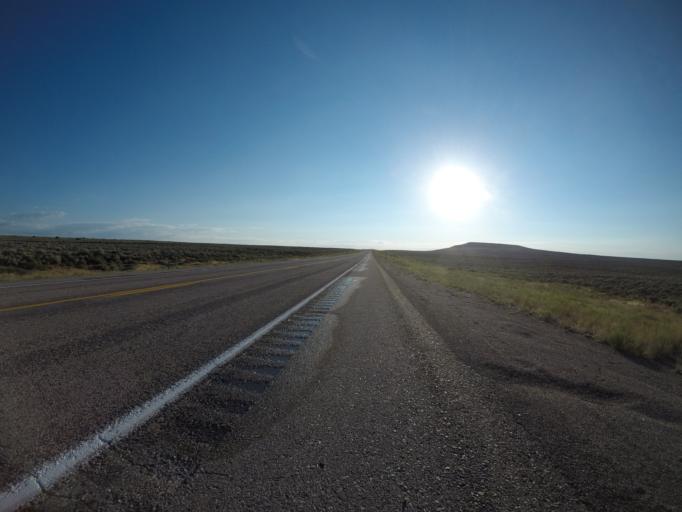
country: US
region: Wyoming
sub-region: Lincoln County
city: Kemmerer
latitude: 41.8822
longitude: -110.4318
